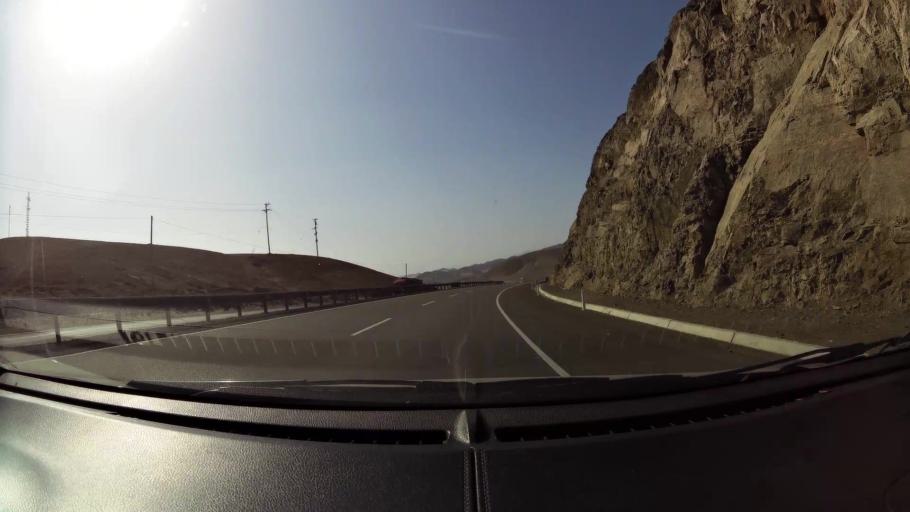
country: PE
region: Ancash
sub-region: Provincia de Huarmey
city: La Caleta Culebras
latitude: -9.9522
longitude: -78.2114
